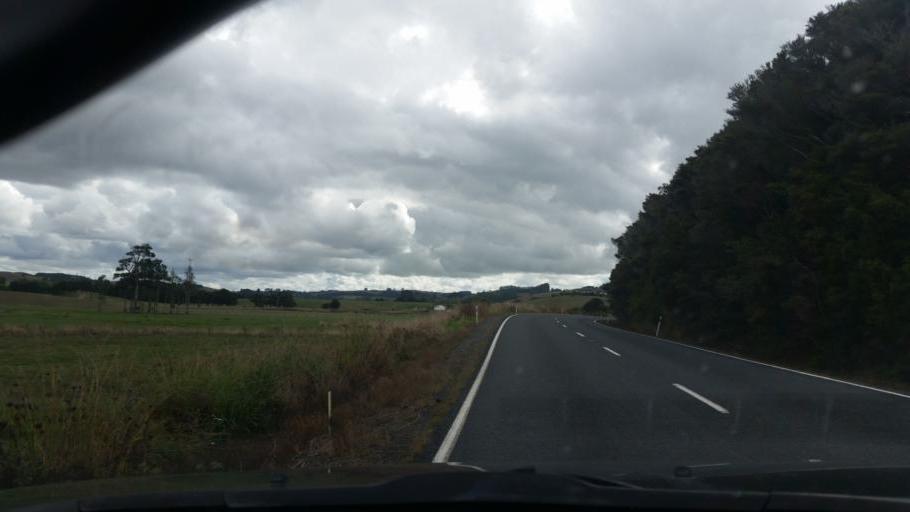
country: NZ
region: Northland
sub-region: Whangarei
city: Ruakaka
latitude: -35.9687
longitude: 174.2901
